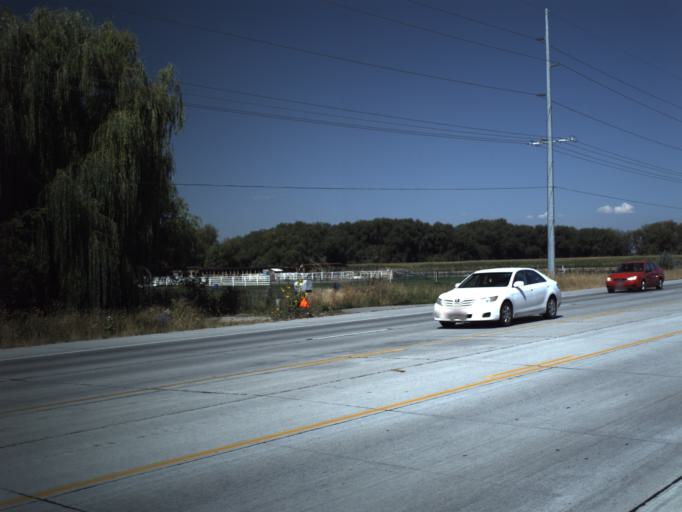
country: US
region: Utah
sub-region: Cache County
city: Logan
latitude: 41.7120
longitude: -111.8601
